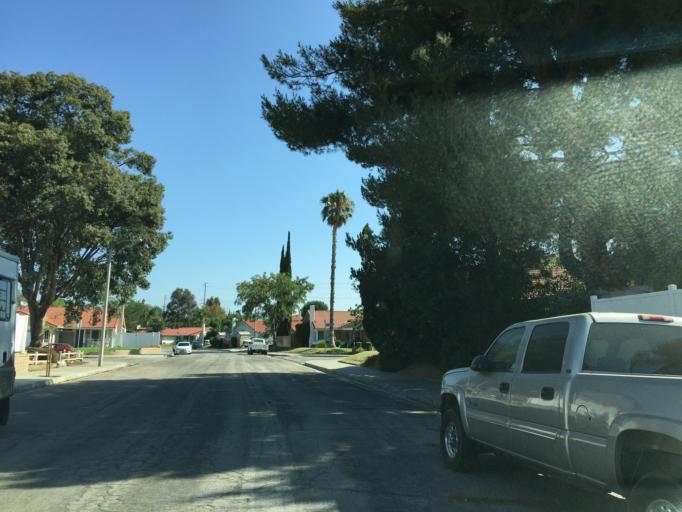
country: US
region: California
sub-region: Los Angeles County
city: Valencia
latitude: 34.4529
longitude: -118.6179
